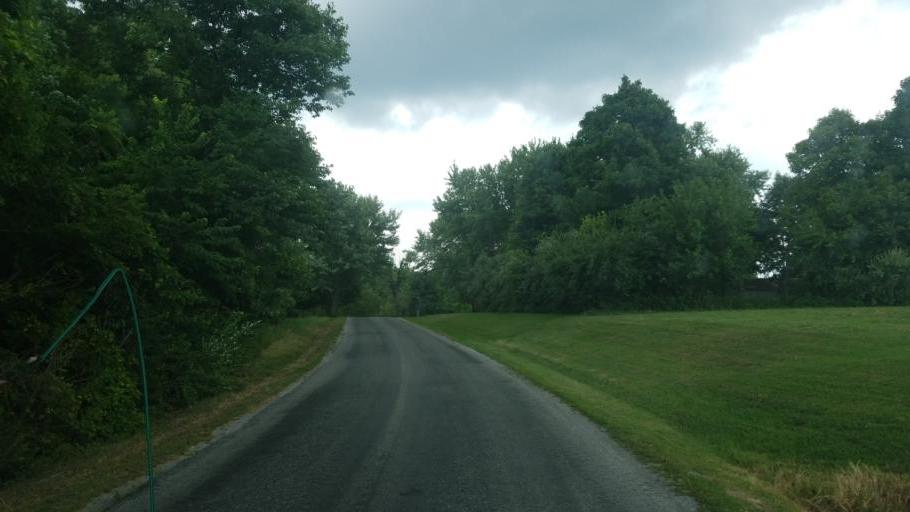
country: US
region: Illinois
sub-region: Jackson County
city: Murphysboro
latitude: 37.7045
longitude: -89.3323
